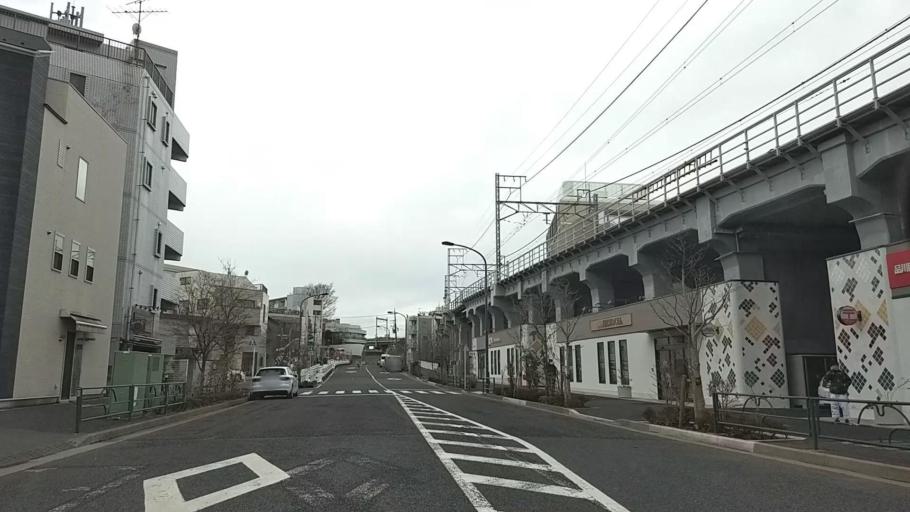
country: JP
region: Kanagawa
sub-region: Kawasaki-shi
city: Kawasaki
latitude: 35.6081
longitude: 139.7290
